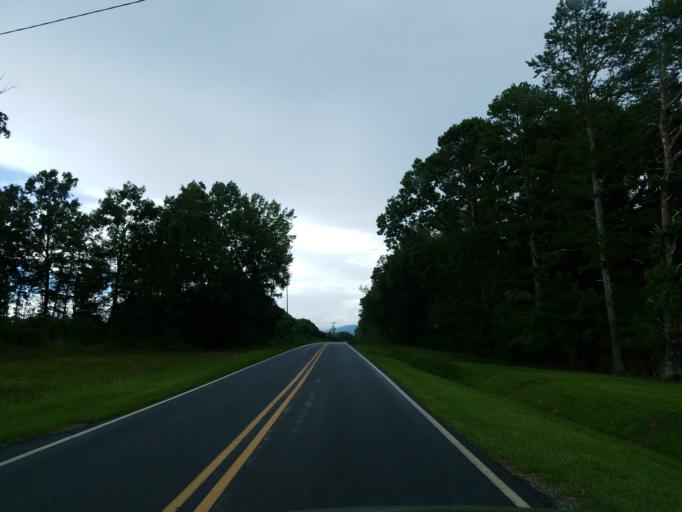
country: US
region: Georgia
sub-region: White County
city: Cleveland
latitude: 34.6036
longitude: -83.8605
